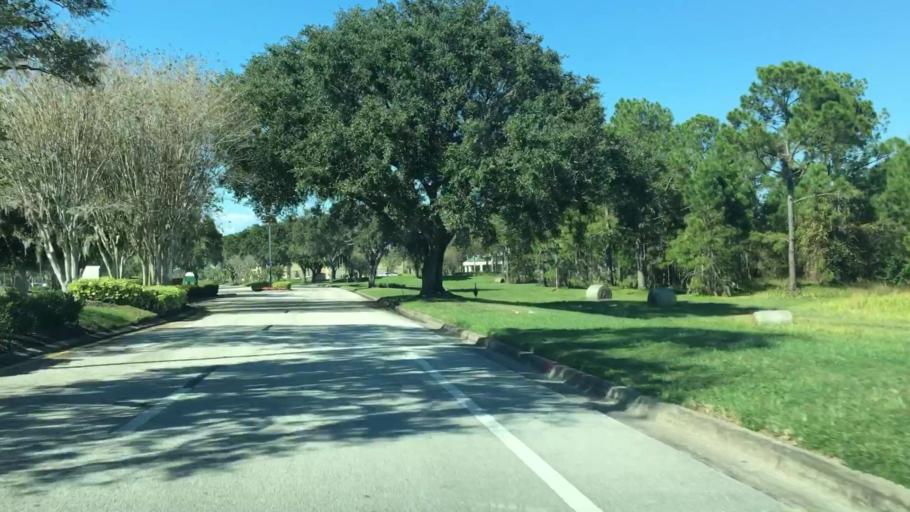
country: US
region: Florida
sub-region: Orange County
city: Conway
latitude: 28.4606
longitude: -81.3022
